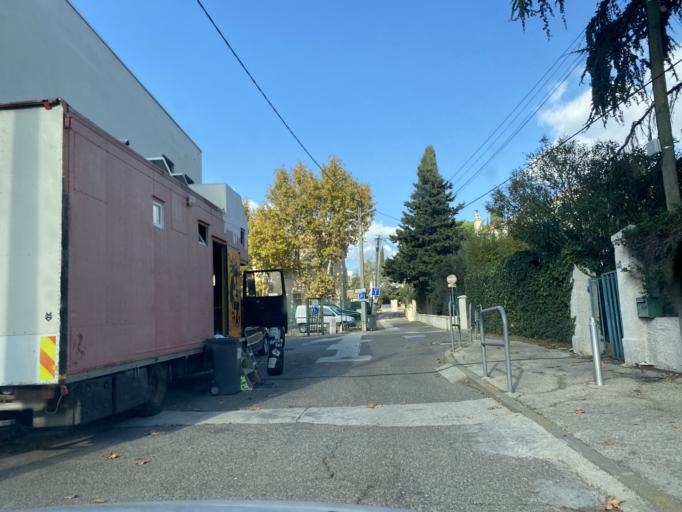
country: FR
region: Provence-Alpes-Cote d'Azur
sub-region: Departement du Var
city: La Seyne-sur-Mer
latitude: 43.1107
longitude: 5.8747
